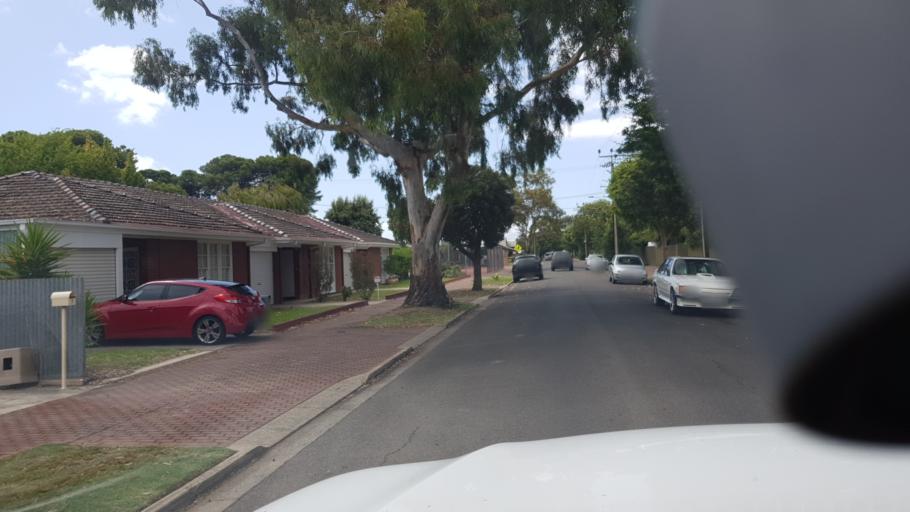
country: AU
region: South Australia
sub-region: Holdfast Bay
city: Glenelg East
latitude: -34.9791
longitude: 138.5256
